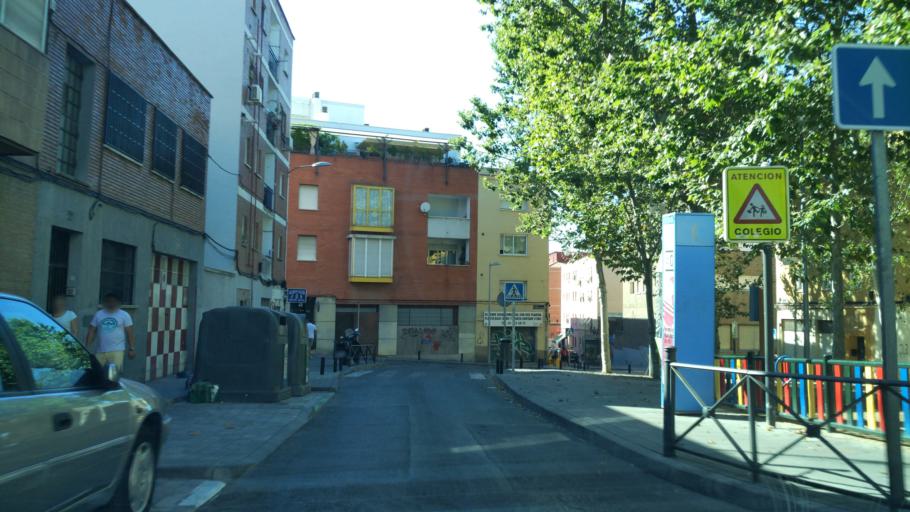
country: ES
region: Madrid
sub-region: Provincia de Madrid
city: Tetuan de las Victorias
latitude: 40.4681
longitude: -3.7003
